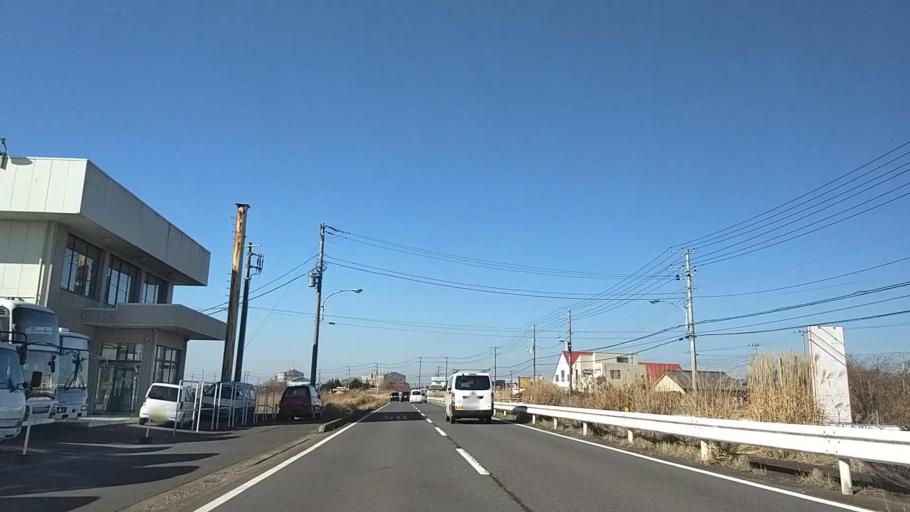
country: JP
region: Chiba
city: Asahi
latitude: 35.7220
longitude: 140.6921
